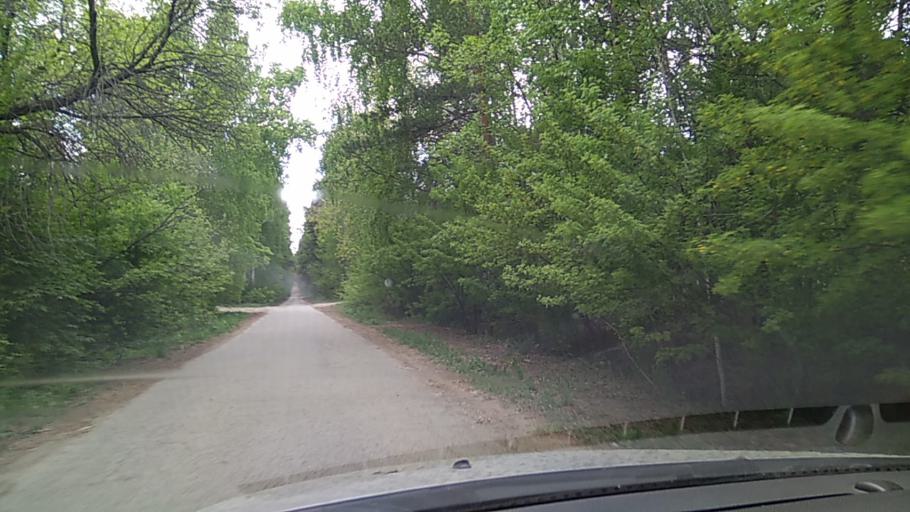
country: RU
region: Sverdlovsk
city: Verkhnyaya Pyshma
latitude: 56.9255
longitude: 60.6015
